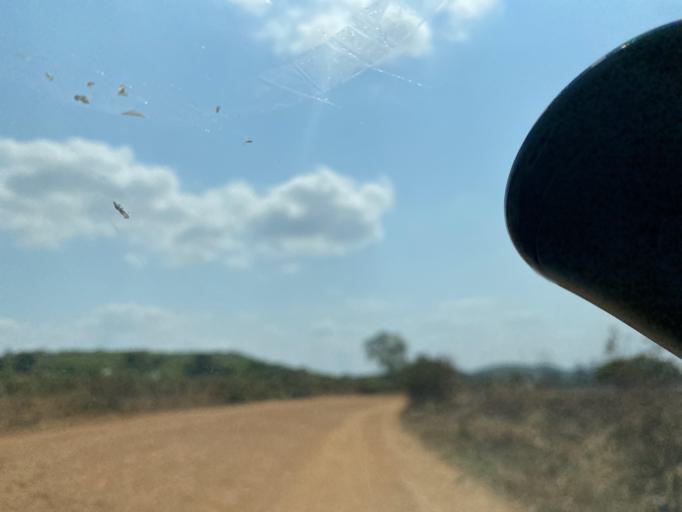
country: ZM
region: Lusaka
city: Chongwe
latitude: -15.6036
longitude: 28.7466
